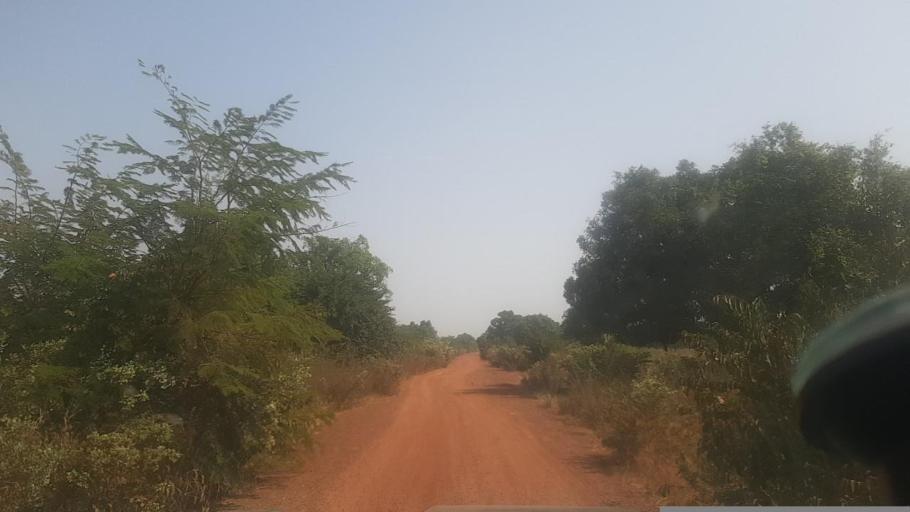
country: ML
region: Segou
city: Bla
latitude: 12.9228
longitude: -6.2639
